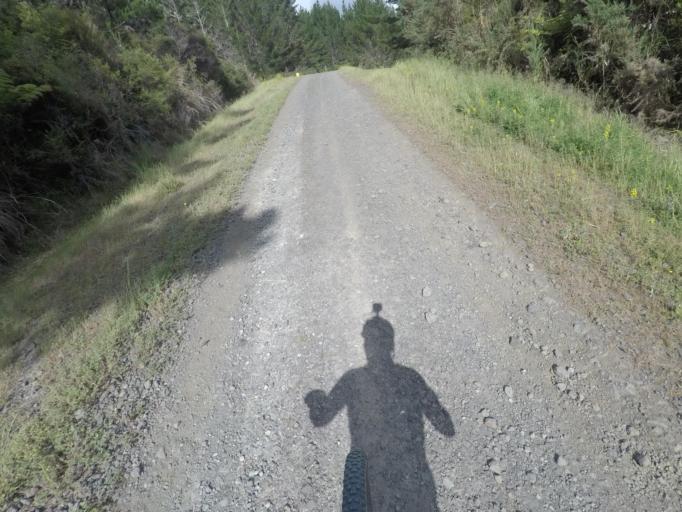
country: NZ
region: Auckland
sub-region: Auckland
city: Muriwai Beach
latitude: -36.7435
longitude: 174.5690
